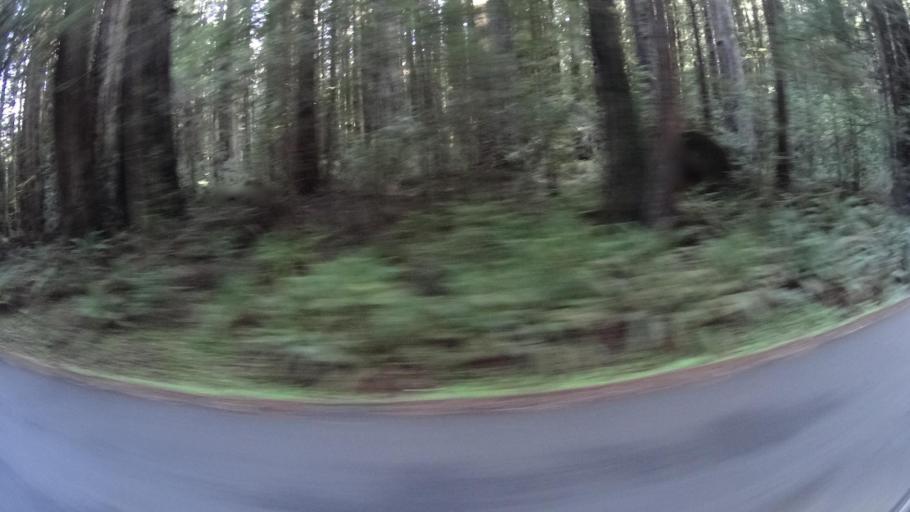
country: US
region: California
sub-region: Humboldt County
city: Rio Dell
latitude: 40.3516
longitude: -124.0038
